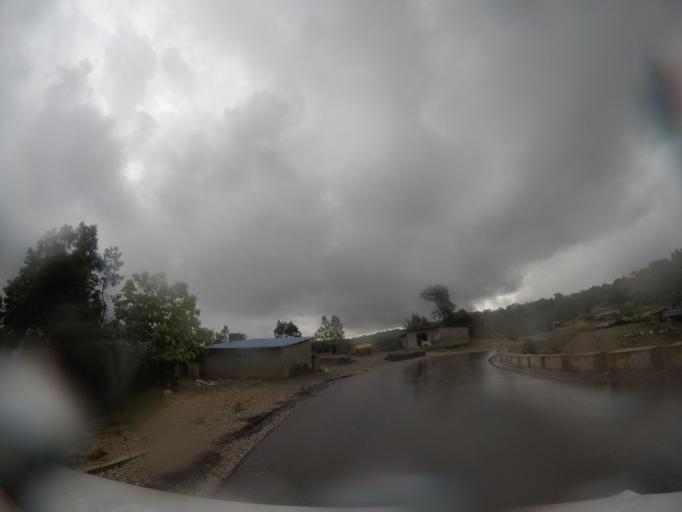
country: TL
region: Baucau
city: Venilale
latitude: -8.6361
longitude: 126.3770
